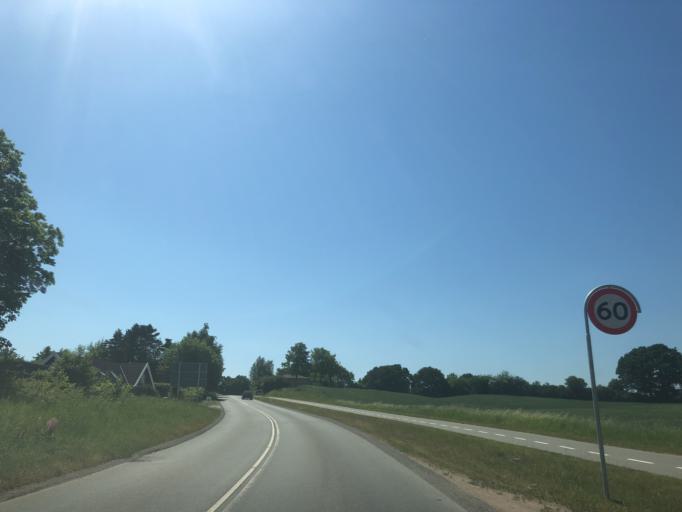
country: DK
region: Capital Region
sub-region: Gribskov Kommune
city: Graested
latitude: 56.0601
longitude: 12.2728
